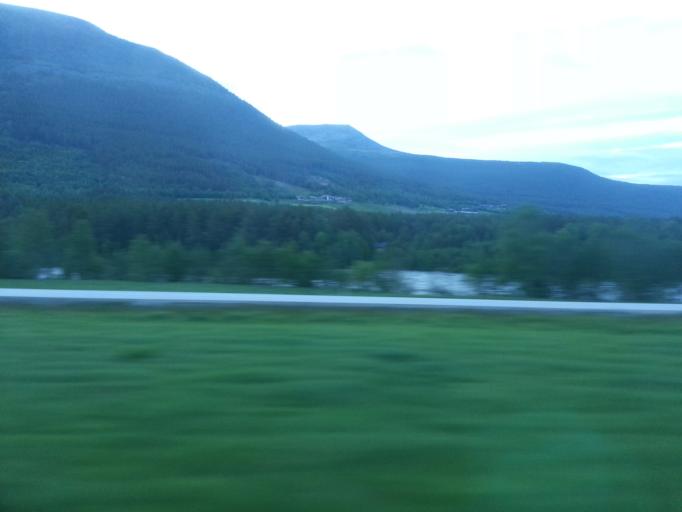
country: NO
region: Oppland
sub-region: Dovre
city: Dovre
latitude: 61.9352
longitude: 9.3033
